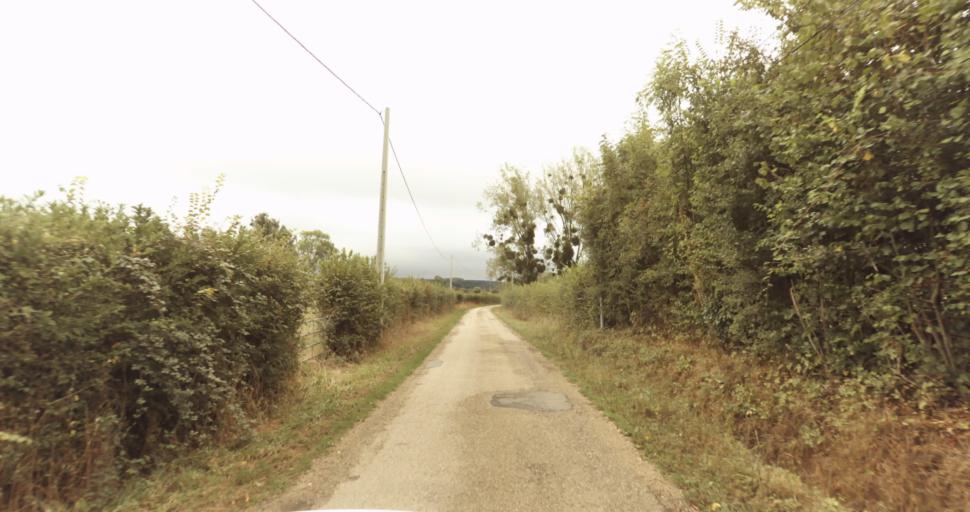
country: FR
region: Lower Normandy
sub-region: Departement de l'Orne
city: Trun
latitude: 48.9209
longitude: 0.0836
